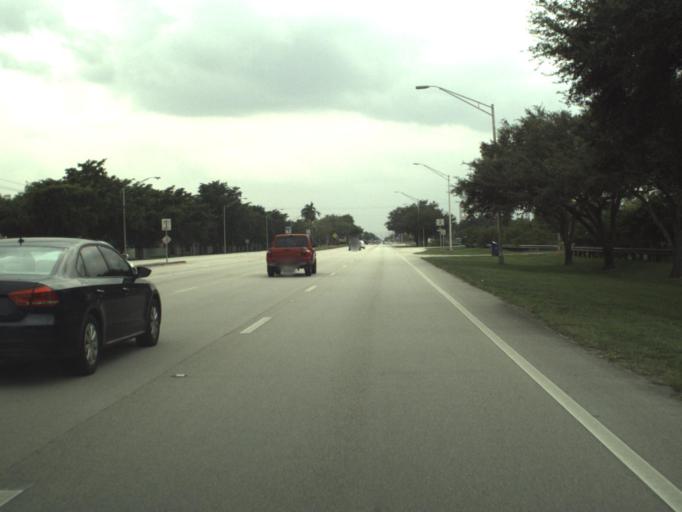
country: US
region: Florida
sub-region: Broward County
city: Sunshine Ranches
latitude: 26.0567
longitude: -80.3135
